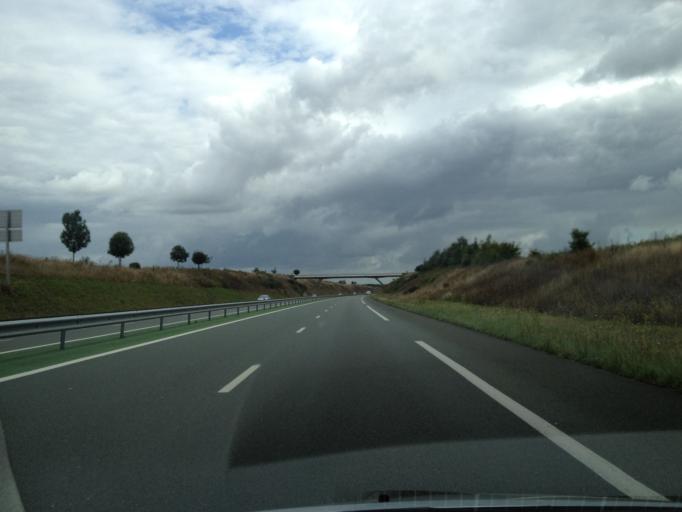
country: FR
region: Pays de la Loire
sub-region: Departement de la Vendee
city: Saint-Fulgent
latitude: 46.8270
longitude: -1.1717
